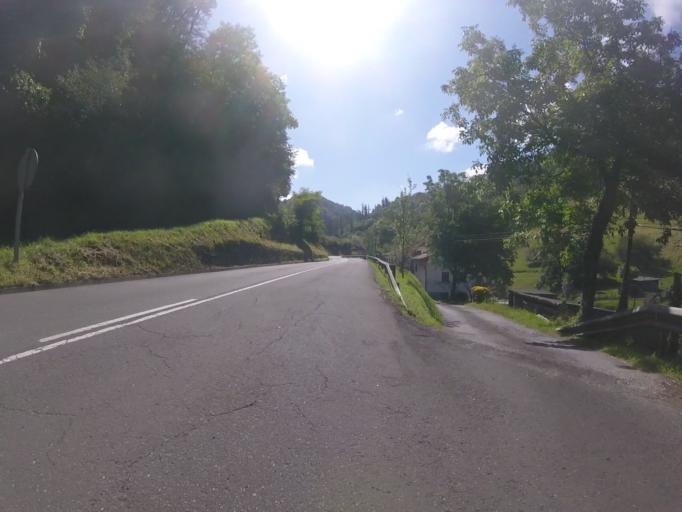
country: ES
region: Basque Country
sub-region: Provincia de Guipuzcoa
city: Azpeitia
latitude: 43.1800
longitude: -2.2318
